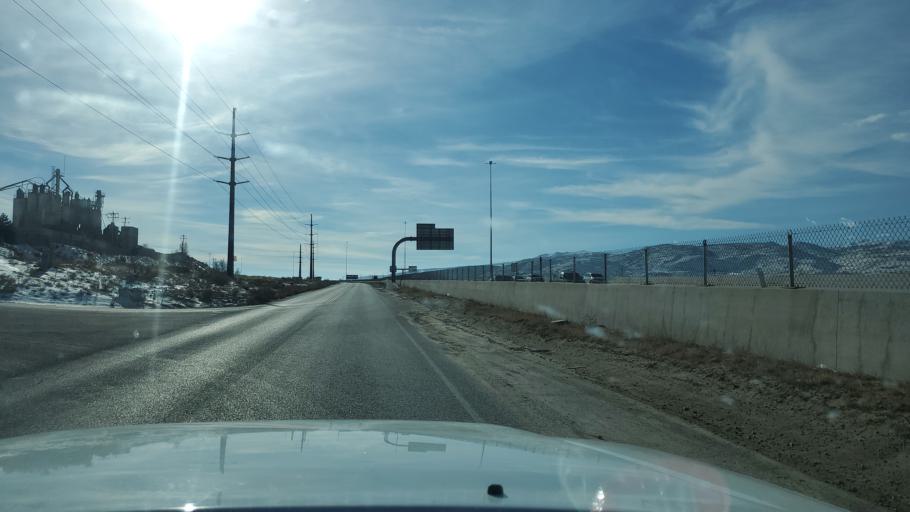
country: US
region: Utah
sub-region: Salt Lake County
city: Bluffdale
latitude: 40.4677
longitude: -111.9106
